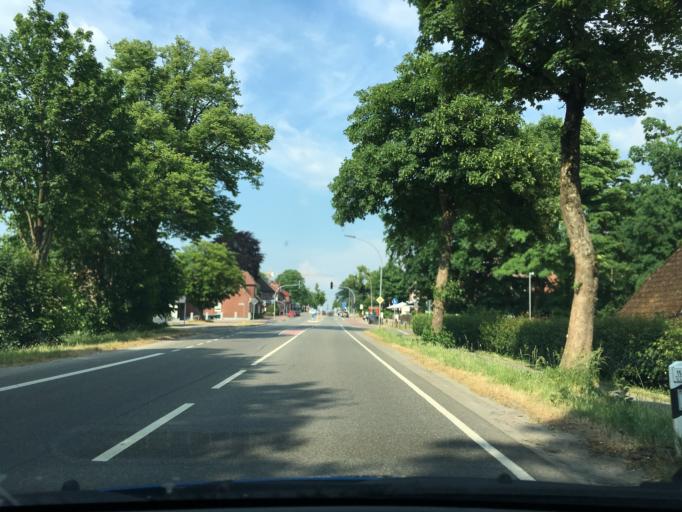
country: DE
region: Lower Saxony
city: Buchholz in der Nordheide
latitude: 53.3780
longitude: 9.8933
